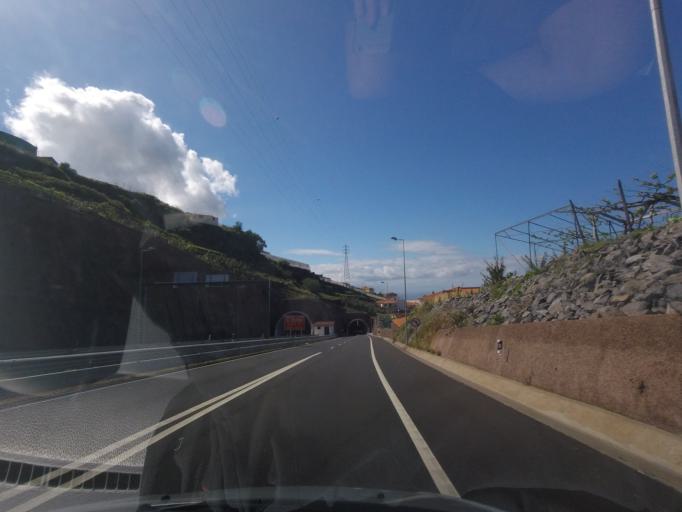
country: PT
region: Madeira
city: Camara de Lobos
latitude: 32.6674
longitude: -16.9703
